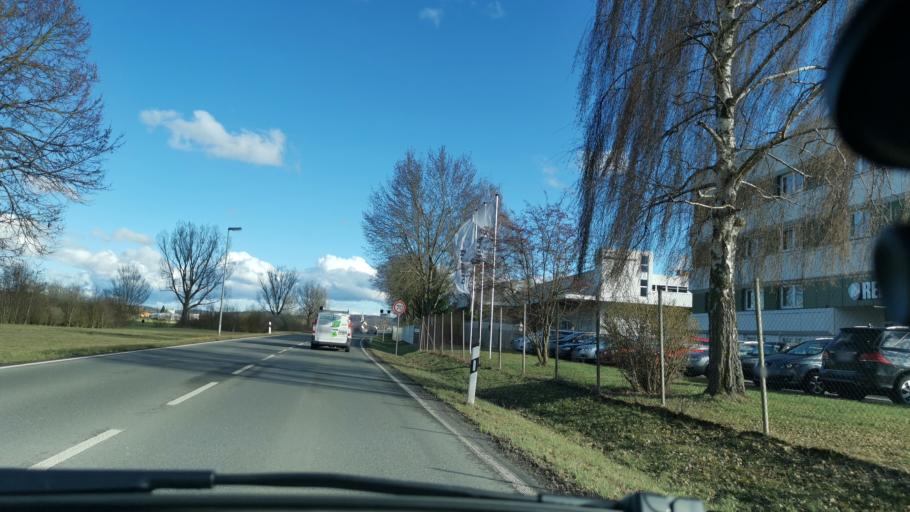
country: DE
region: Baden-Wuerttemberg
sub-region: Regierungsbezirk Stuttgart
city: Renningen
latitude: 48.7711
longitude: 8.9088
